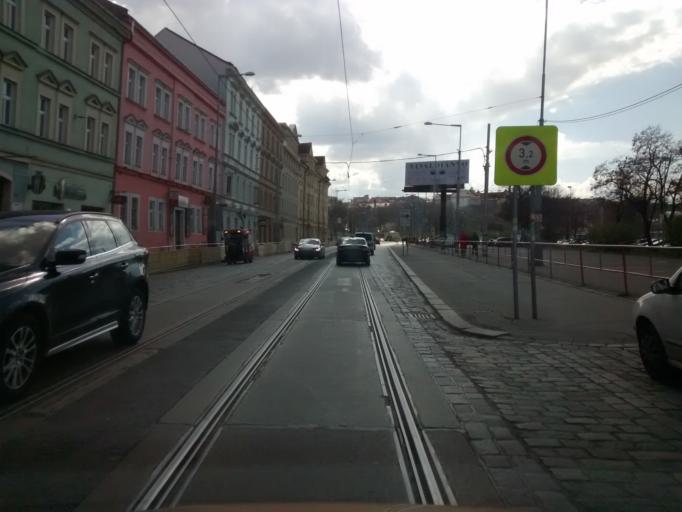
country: CZ
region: Praha
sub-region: Praha 8
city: Karlin
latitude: 50.1063
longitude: 14.4349
